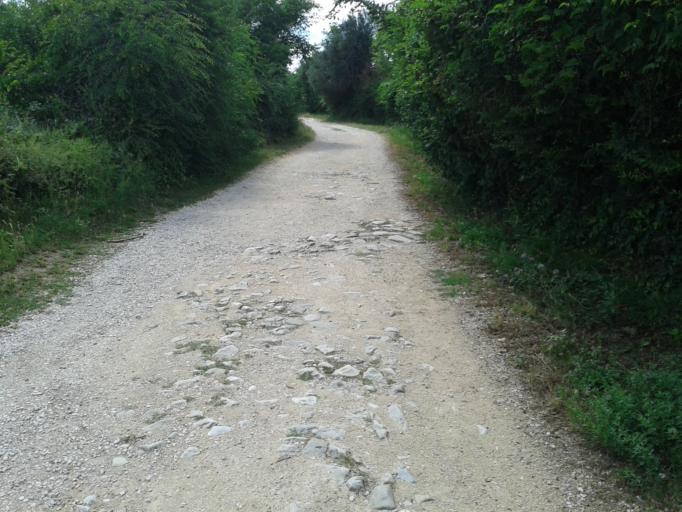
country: HR
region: Splitsko-Dalmatinska
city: Vranjic
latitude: 43.5390
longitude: 16.4785
